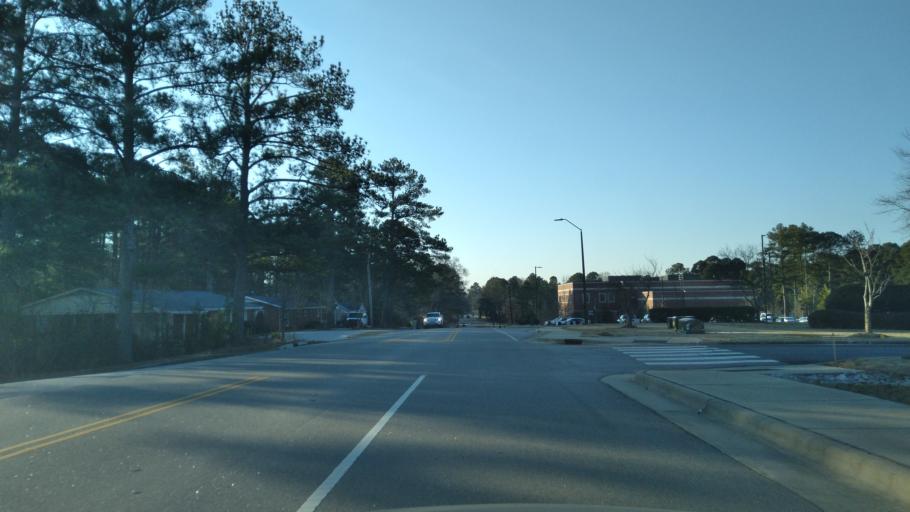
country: US
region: North Carolina
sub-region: Wake County
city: Garner
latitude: 35.7075
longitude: -78.6200
